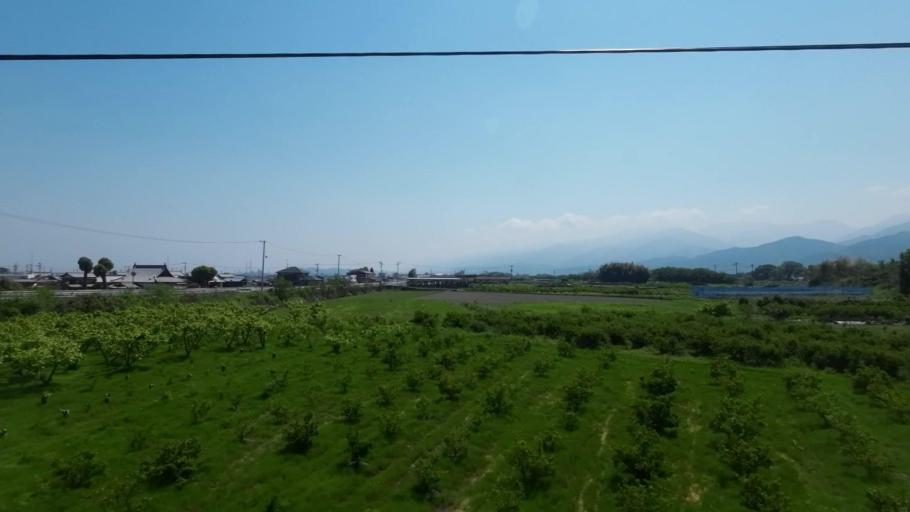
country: JP
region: Ehime
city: Saijo
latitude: 33.9082
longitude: 133.0992
